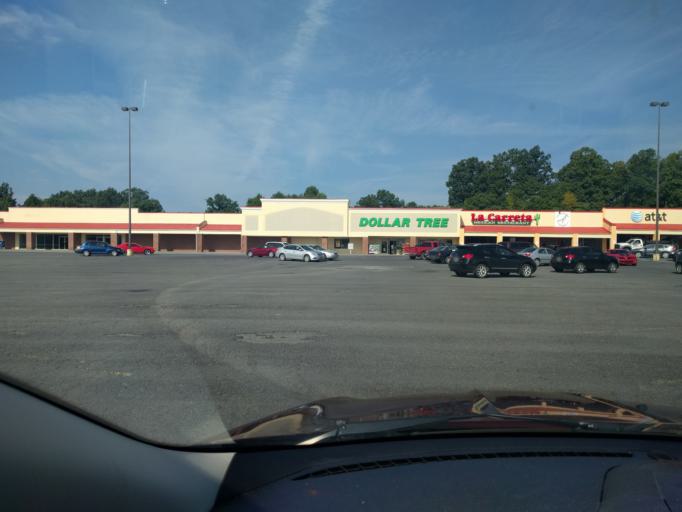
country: US
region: West Virginia
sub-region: Nicholas County
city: Summersville
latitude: 38.2977
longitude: -80.8344
